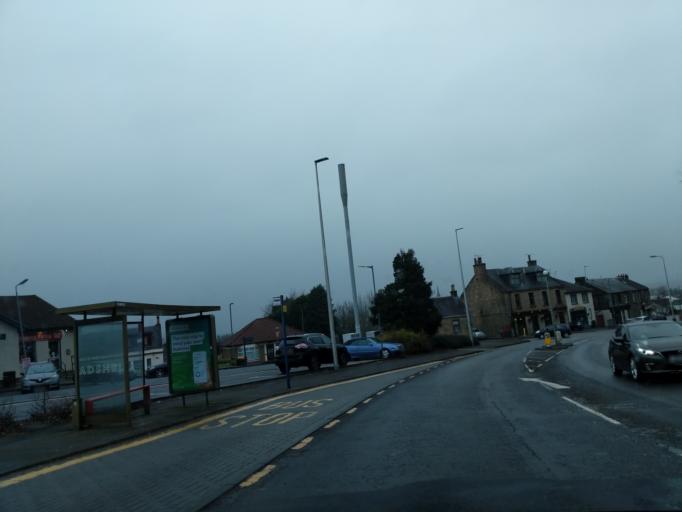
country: GB
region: Scotland
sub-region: Falkirk
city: Falkirk
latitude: 55.9933
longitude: -3.7893
